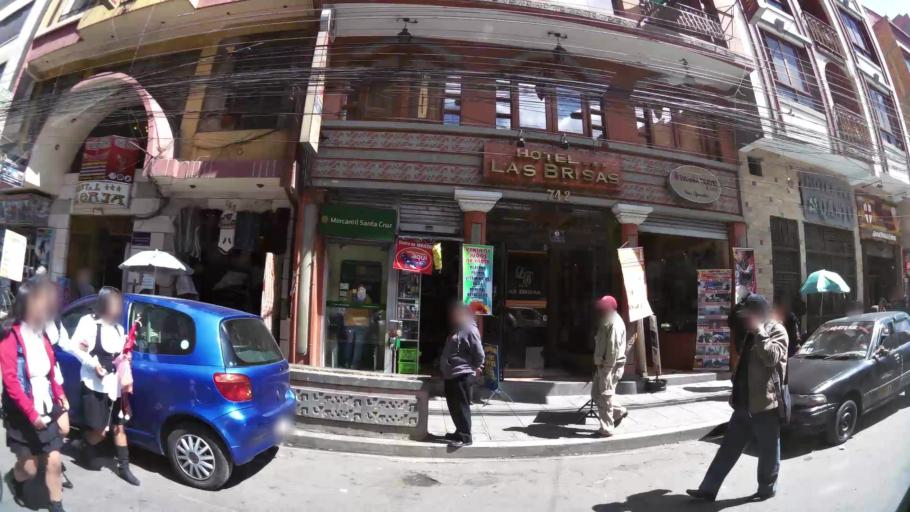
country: BO
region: La Paz
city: La Paz
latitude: -16.4961
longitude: -68.1399
